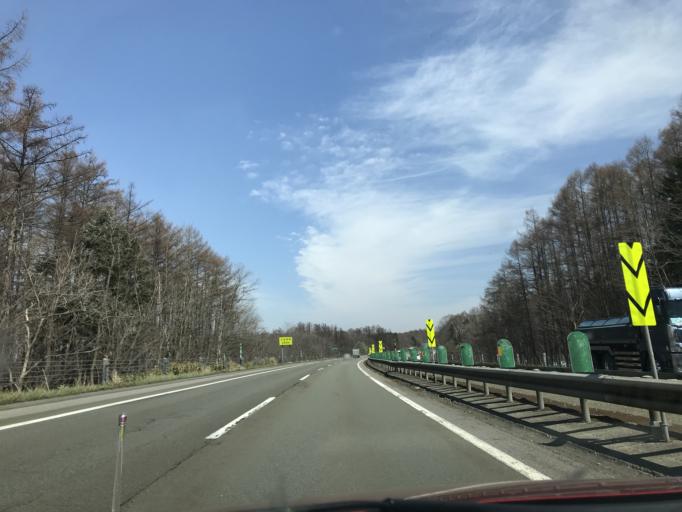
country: JP
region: Hokkaido
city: Bibai
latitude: 43.2784
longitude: 141.8518
